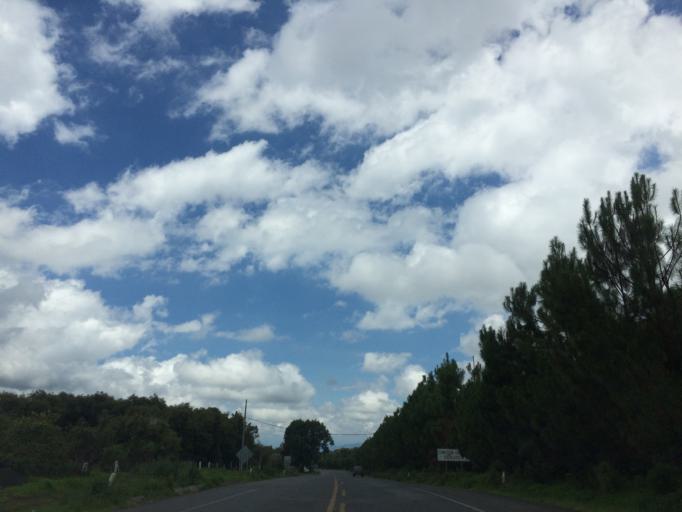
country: MX
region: Michoacan
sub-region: Uruapan
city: Nuevo Zirosto
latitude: 19.5485
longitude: -102.3372
